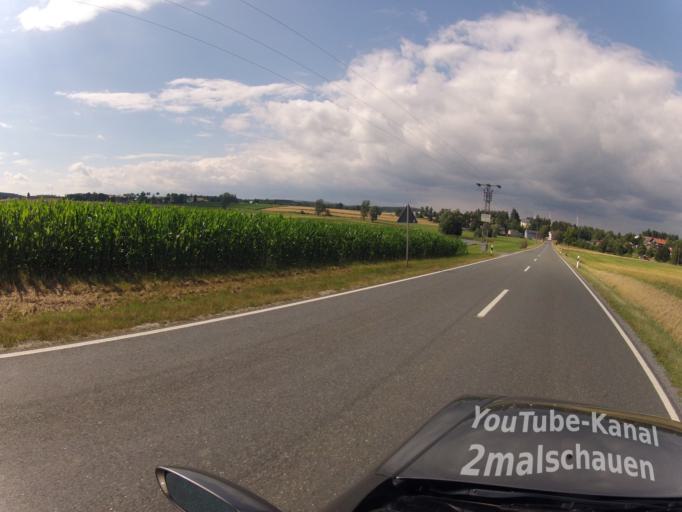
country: DE
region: Bavaria
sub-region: Upper Franconia
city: Roslau
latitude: 50.0754
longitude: 11.9739
